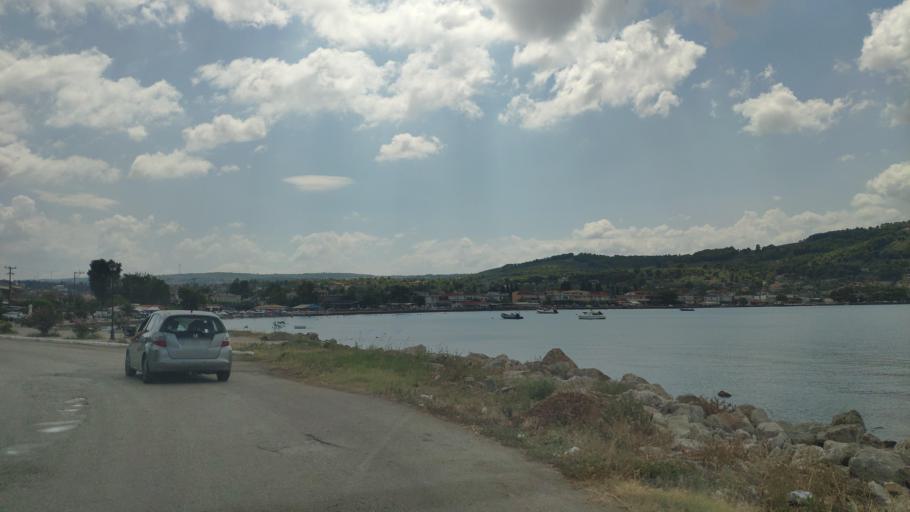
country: GR
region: Central Greece
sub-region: Nomos Fthiotidos
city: Malesina
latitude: 38.6575
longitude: 23.1900
